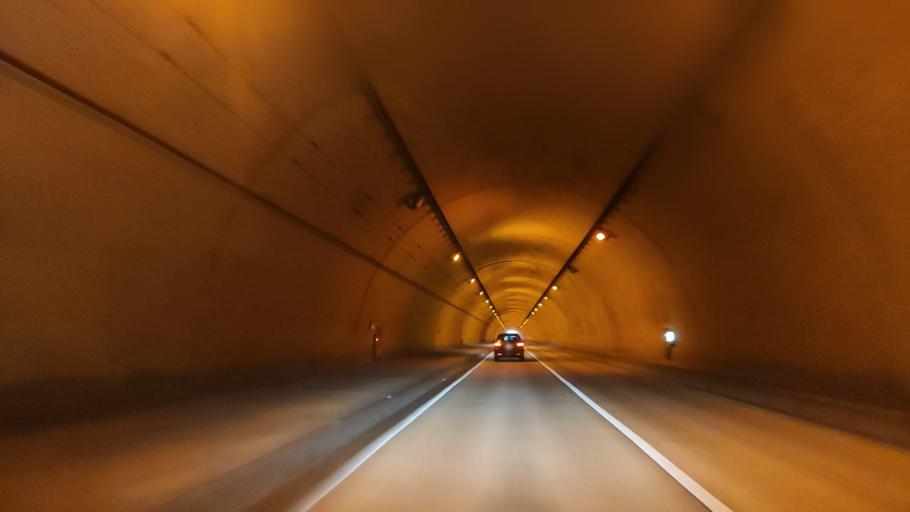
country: JP
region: Ehime
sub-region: Shikoku-chuo Shi
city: Matsuyama
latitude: 33.8828
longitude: 132.7099
